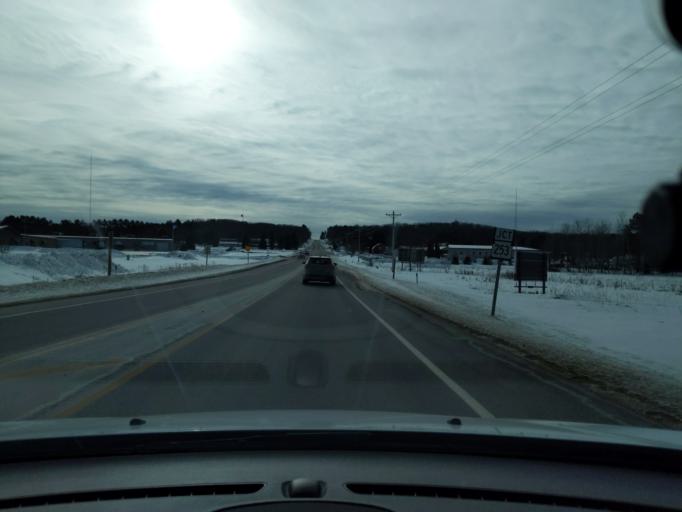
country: US
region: Wisconsin
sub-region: Washburn County
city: Spooner
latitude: 45.8125
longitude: -91.8979
